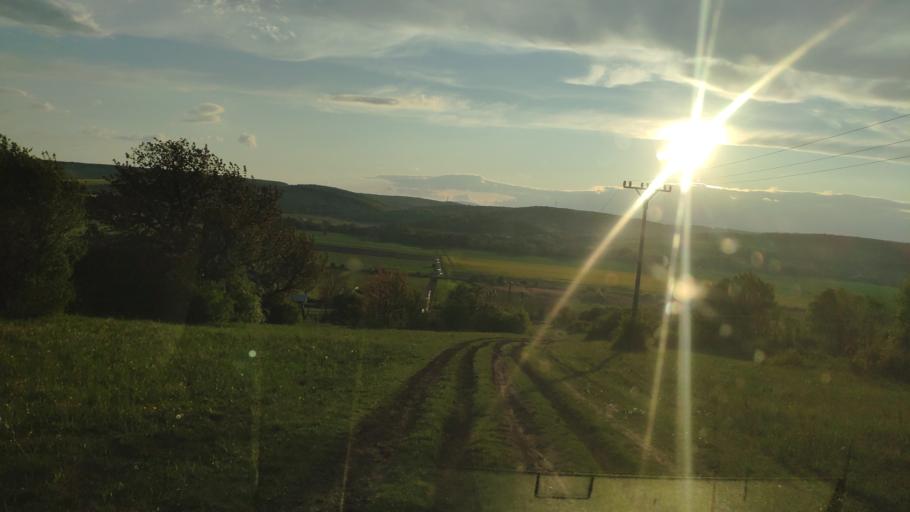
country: SK
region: Kosicky
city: Kosice
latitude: 48.7155
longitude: 21.3518
